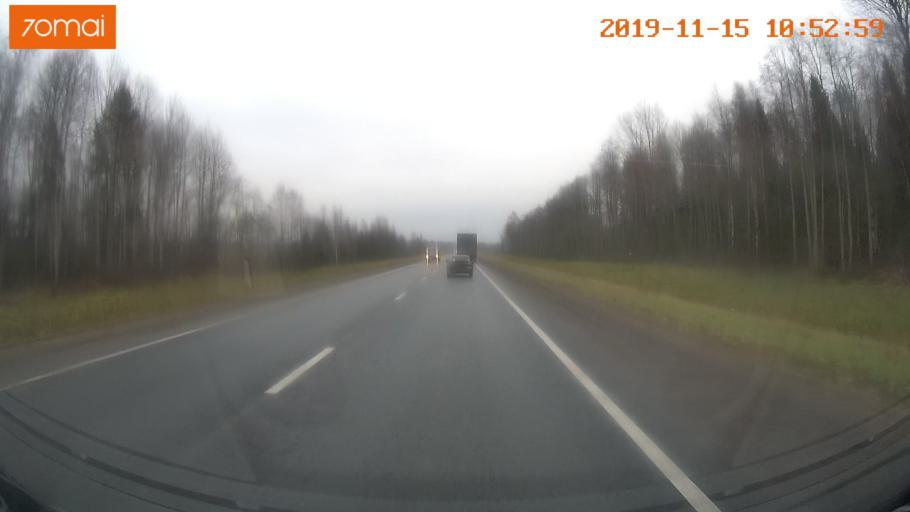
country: RU
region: Vologda
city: Chebsara
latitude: 59.1714
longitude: 38.7445
